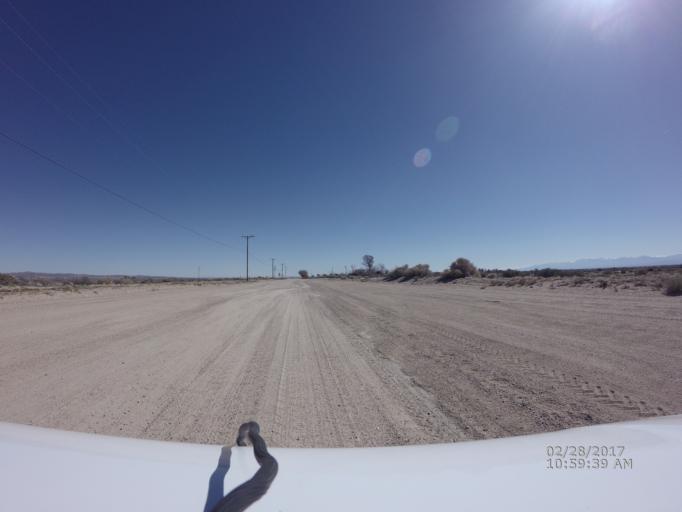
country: US
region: California
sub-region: Kern County
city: Rosamond
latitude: 34.8059
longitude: -118.1872
